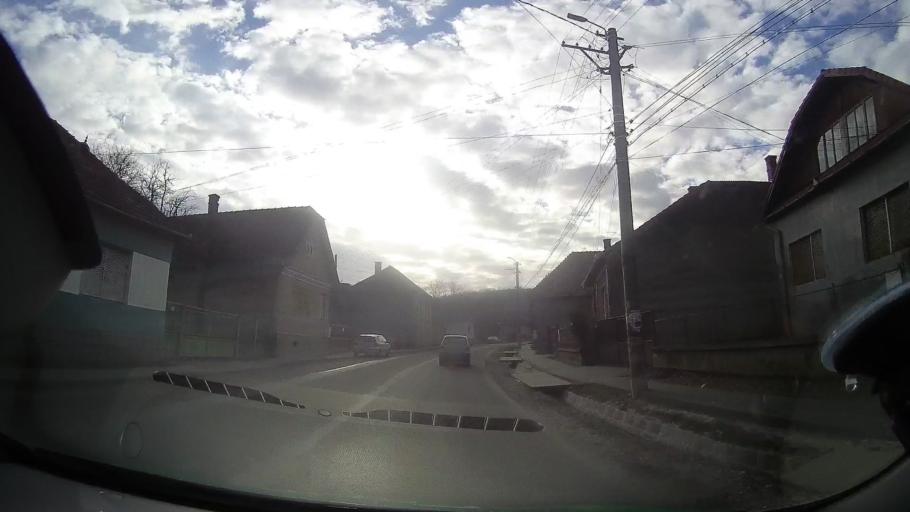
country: RO
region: Cluj
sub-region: Comuna Savadisla
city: Savadisla
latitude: 46.6753
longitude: 23.4566
